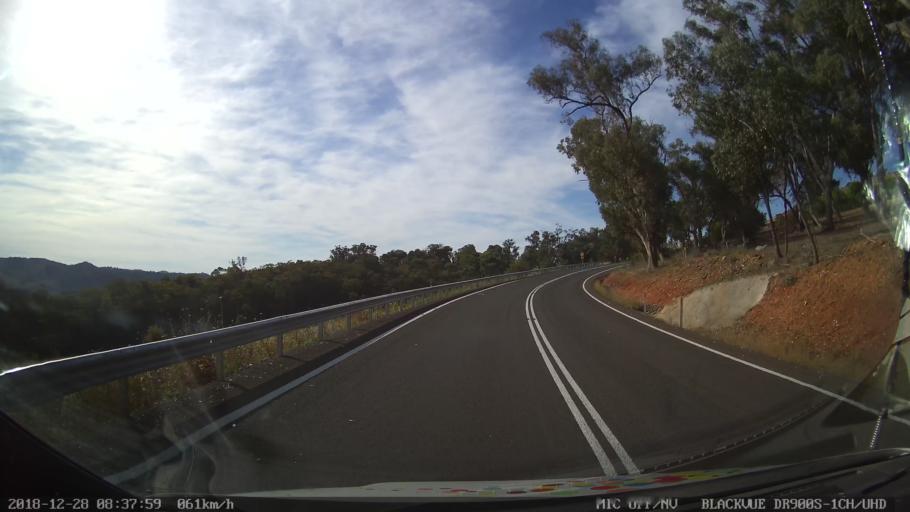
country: AU
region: New South Wales
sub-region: Blayney
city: Blayney
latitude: -33.9998
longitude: 149.3144
